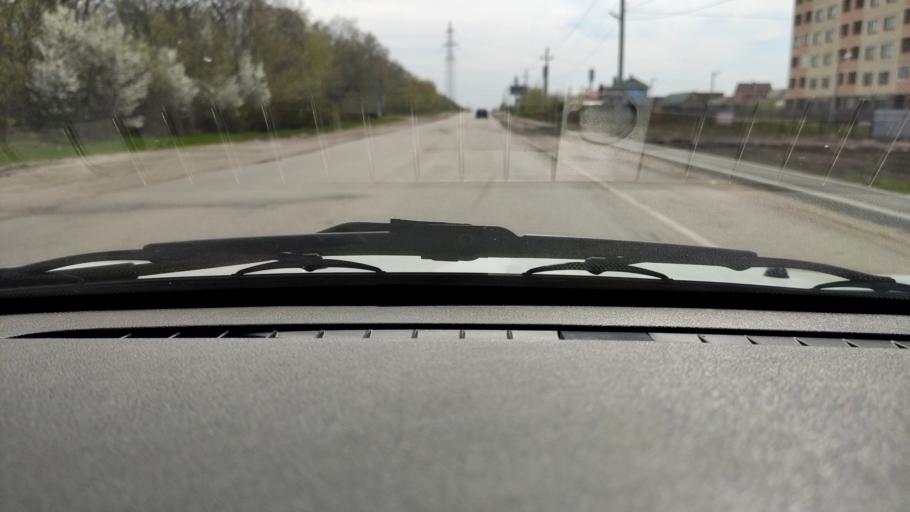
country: RU
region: Voronezj
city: Novaya Usman'
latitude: 51.6286
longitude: 39.3342
